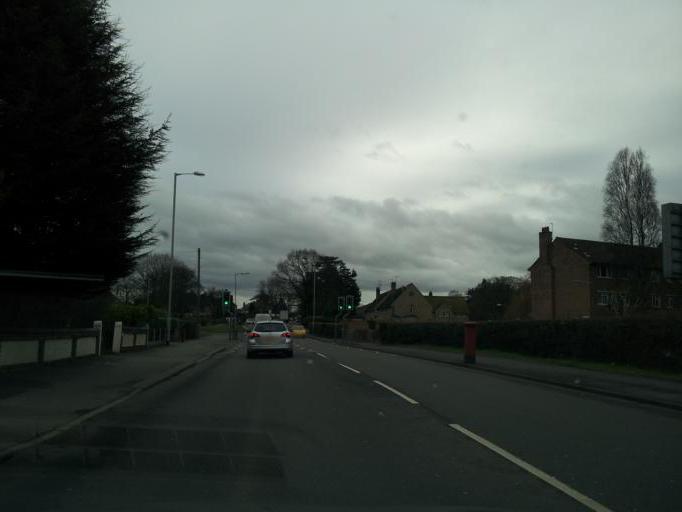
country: GB
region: England
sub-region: Staffordshire
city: Stafford
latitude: 52.7828
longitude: -2.1144
